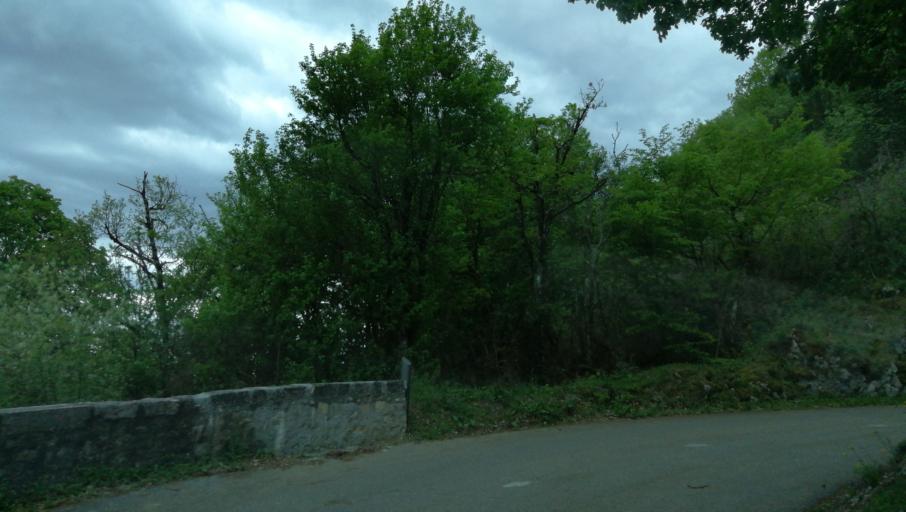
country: FR
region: Rhone-Alpes
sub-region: Departement de la Savoie
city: Chatillon
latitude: 45.7564
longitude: 5.8294
